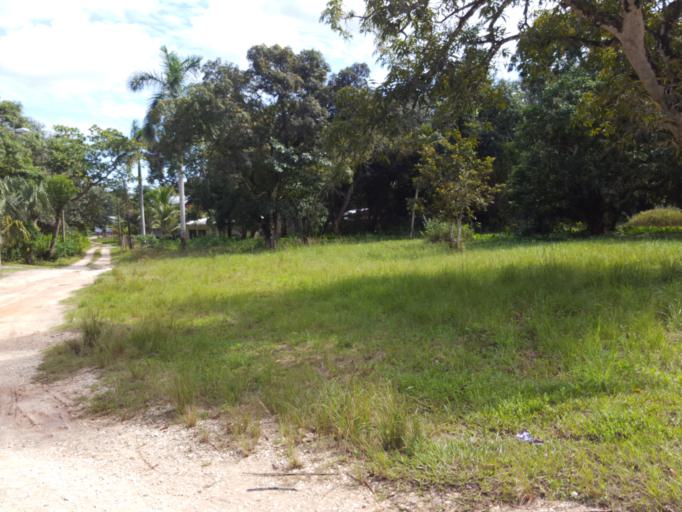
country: BZ
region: Belize
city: Belize City
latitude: 17.5708
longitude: -88.4036
